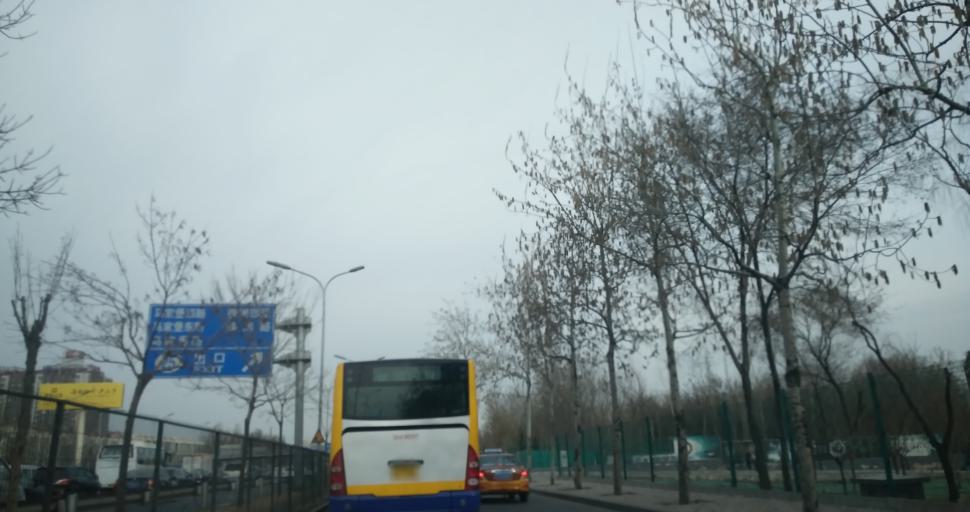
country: CN
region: Beijing
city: Huaxiang
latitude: 39.8295
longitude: 116.3569
